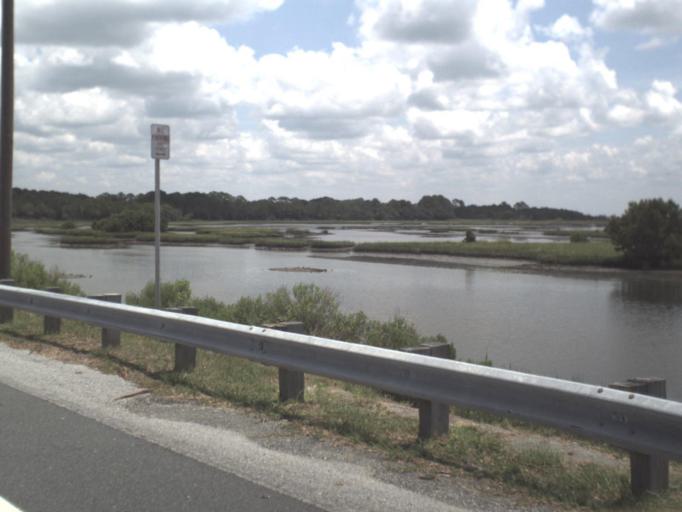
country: US
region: Florida
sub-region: Levy County
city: Chiefland
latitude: 29.1673
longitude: -83.0270
